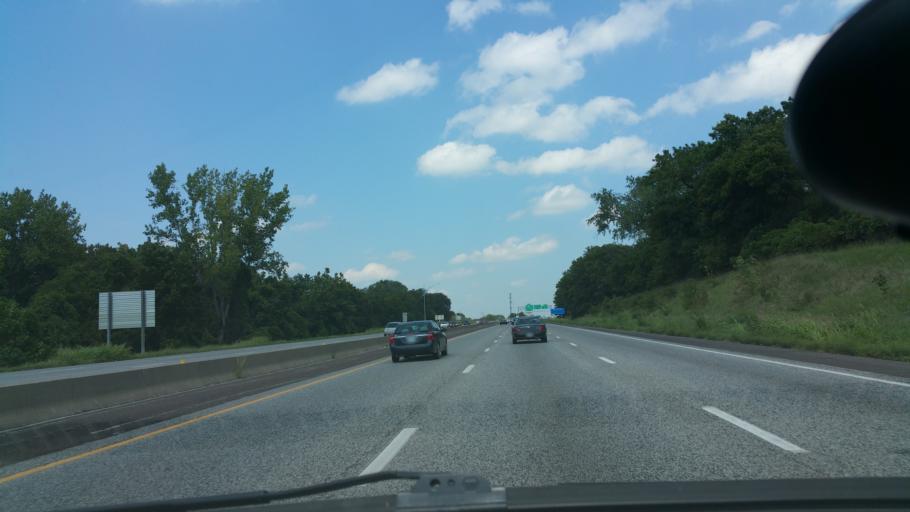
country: US
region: Missouri
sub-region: Clay County
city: North Kansas City
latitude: 39.1586
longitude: -94.5595
